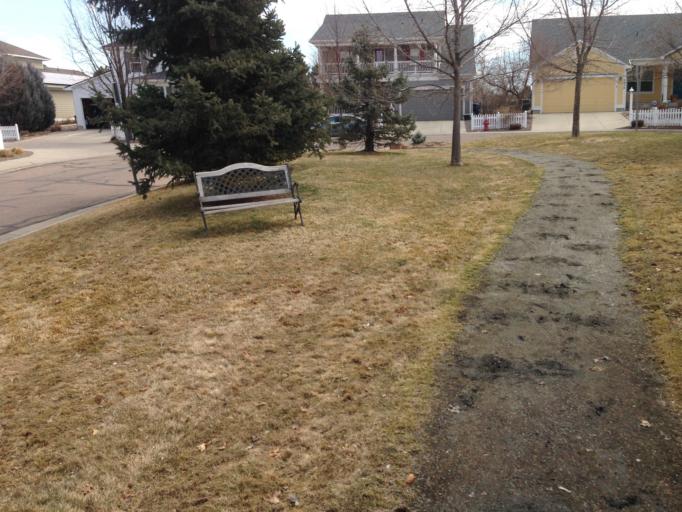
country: US
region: Colorado
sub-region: Boulder County
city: Louisville
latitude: 40.0057
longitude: -105.1327
